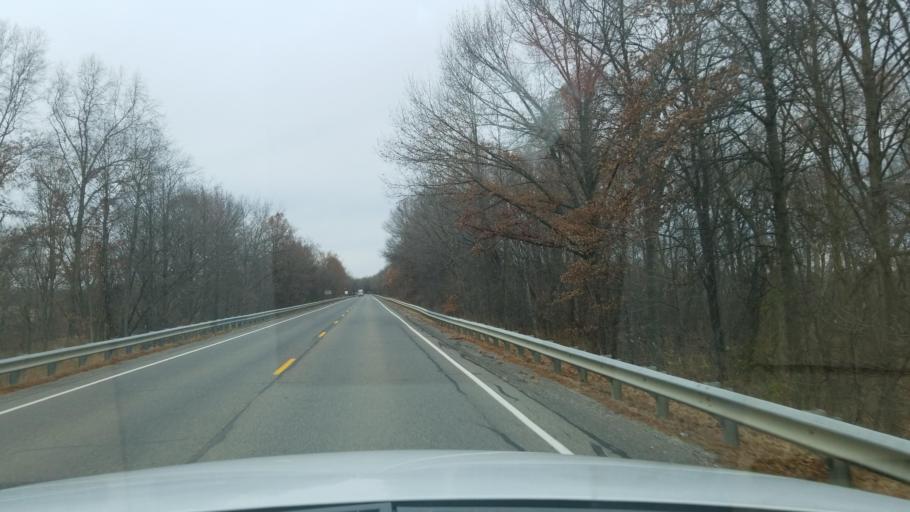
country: US
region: Indiana
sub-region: Posey County
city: Mount Vernon
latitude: 37.9386
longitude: -88.0122
